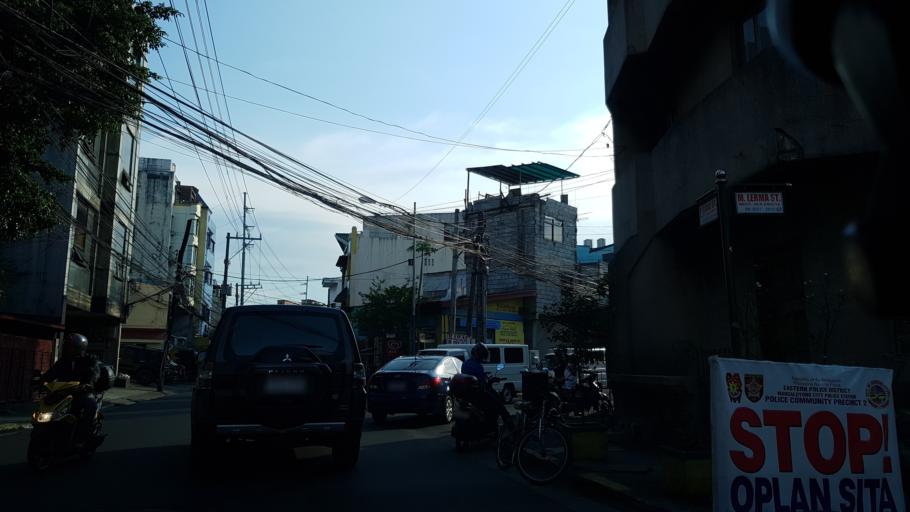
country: PH
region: Metro Manila
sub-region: Mandaluyong
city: Mandaluyong City
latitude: 14.5791
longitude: 121.0280
